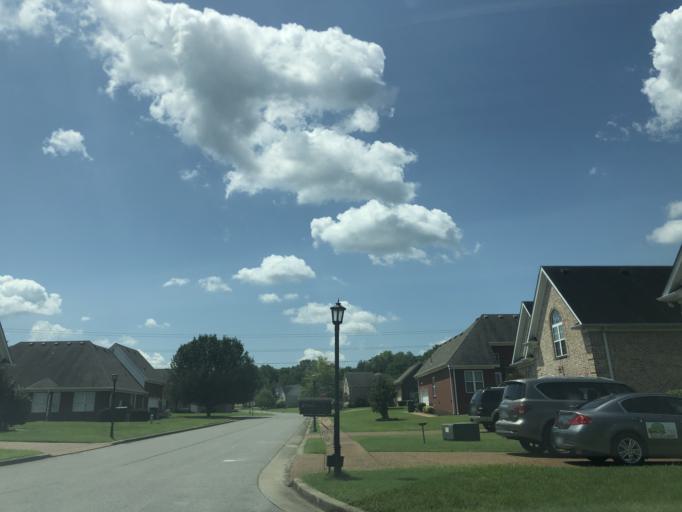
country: US
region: Tennessee
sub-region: Wilson County
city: Green Hill
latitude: 36.1613
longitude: -86.5841
